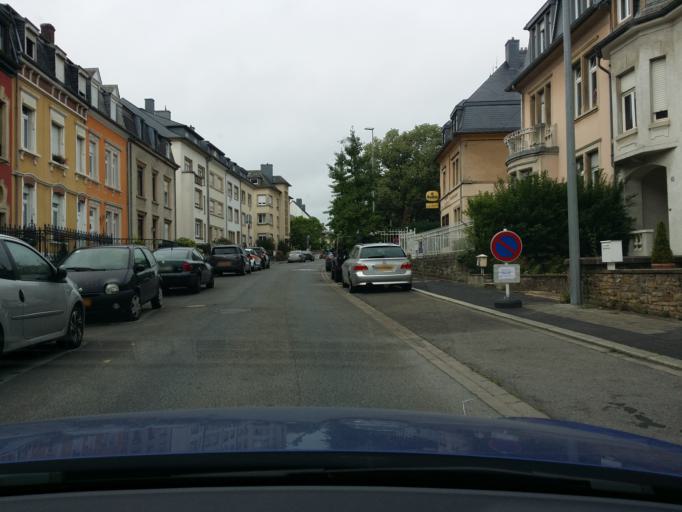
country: LU
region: Luxembourg
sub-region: Canton de Luxembourg
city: Luxembourg
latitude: 49.6229
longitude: 6.1228
